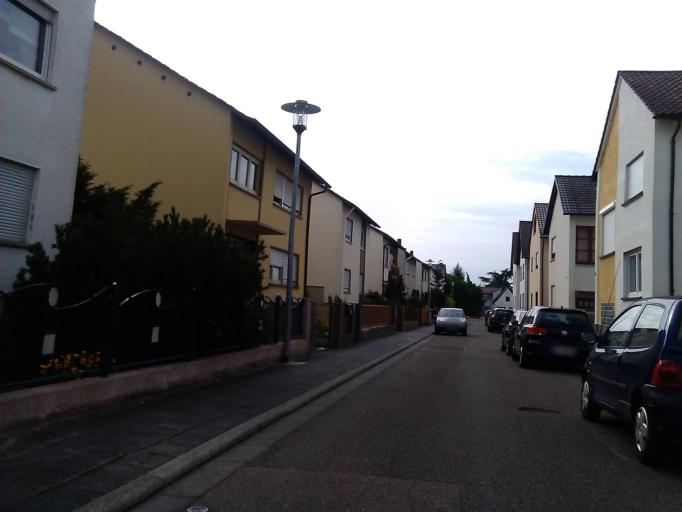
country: DE
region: Rheinland-Pfalz
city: Schifferstadt
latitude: 49.3789
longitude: 8.3838
